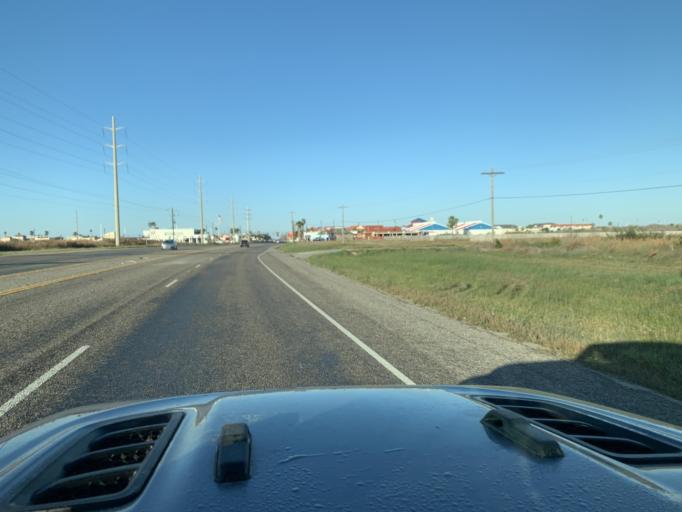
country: US
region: Texas
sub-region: Nueces County
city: Corpus Christi
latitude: 27.6180
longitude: -97.2179
